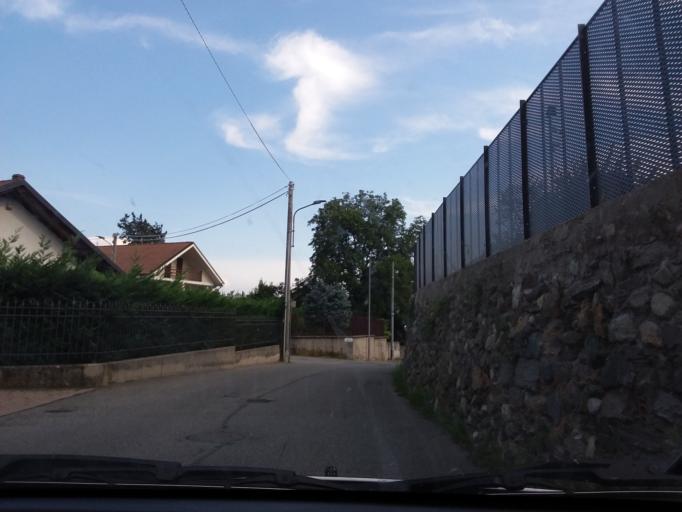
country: IT
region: Piedmont
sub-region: Provincia di Torino
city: Rivoli
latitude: 45.0763
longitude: 7.5248
